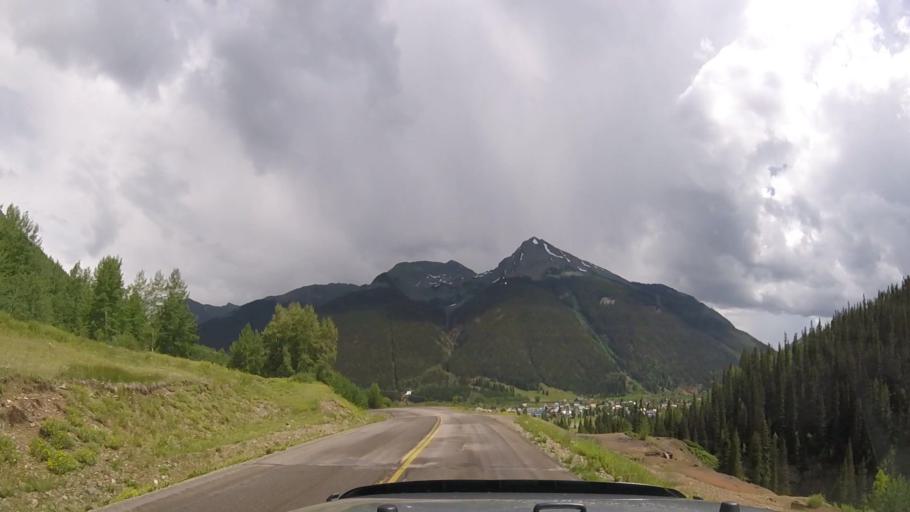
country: US
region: Colorado
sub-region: San Juan County
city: Silverton
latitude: 37.8211
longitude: -107.6632
